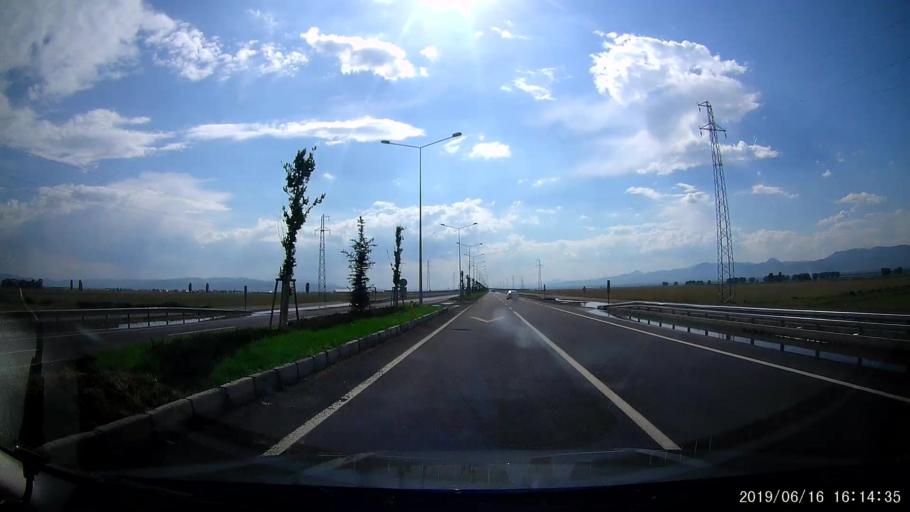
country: TR
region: Erzurum
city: Erzurum
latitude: 39.9609
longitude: 41.2454
